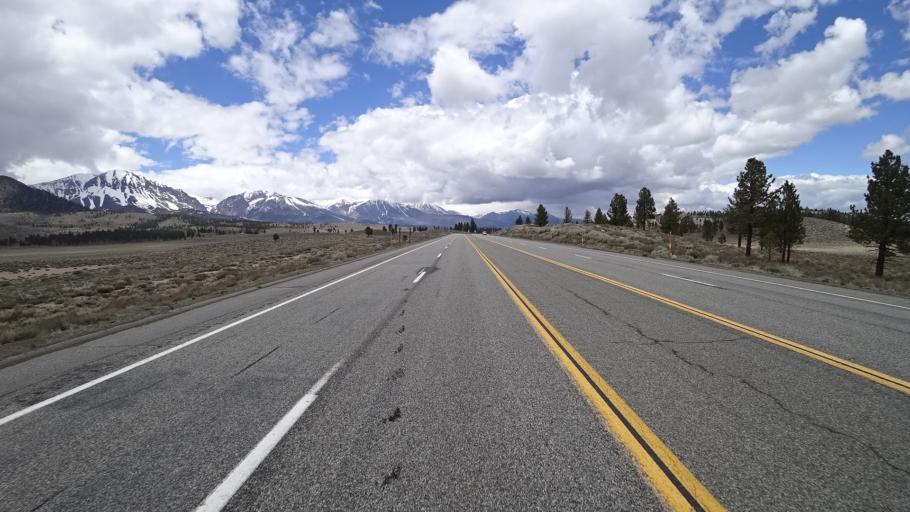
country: US
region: California
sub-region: Mono County
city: Mammoth Lakes
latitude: 37.8148
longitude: -119.0563
